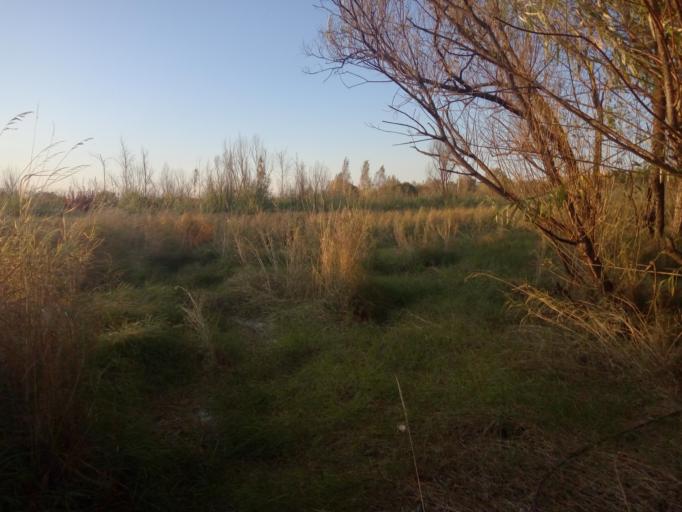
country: RU
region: Khabarovsk Krai
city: Khor
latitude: 47.7034
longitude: 134.9643
